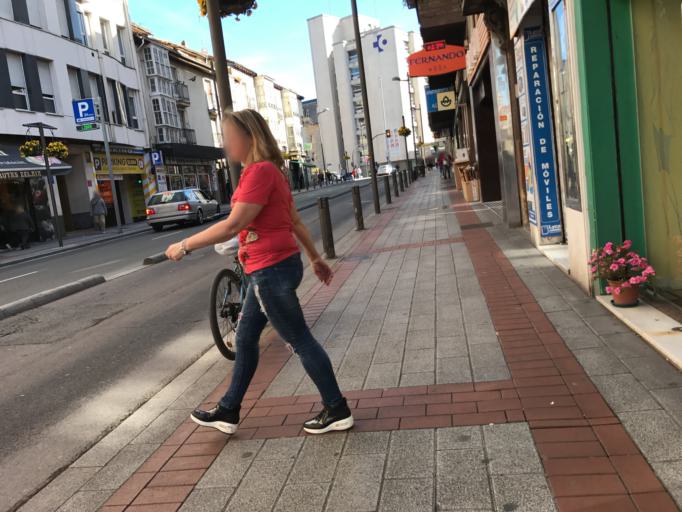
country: ES
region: Basque Country
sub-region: Provincia de Alava
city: Gasteiz / Vitoria
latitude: 42.8477
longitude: -2.6680
